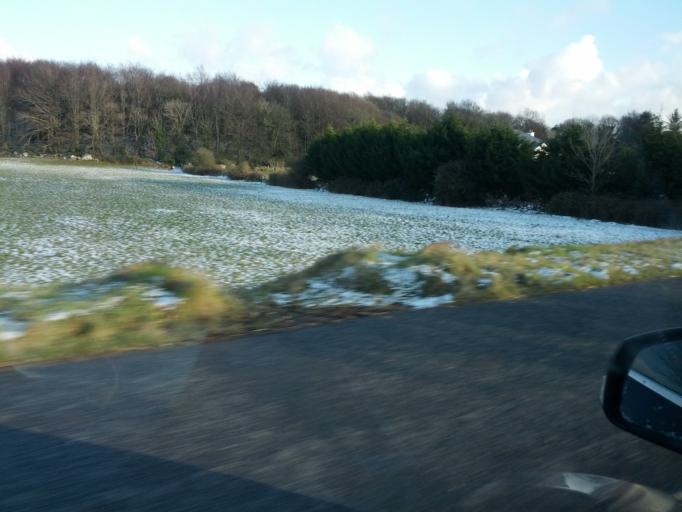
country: IE
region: Connaught
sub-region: County Galway
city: Gort
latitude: 53.1499
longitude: -8.8054
